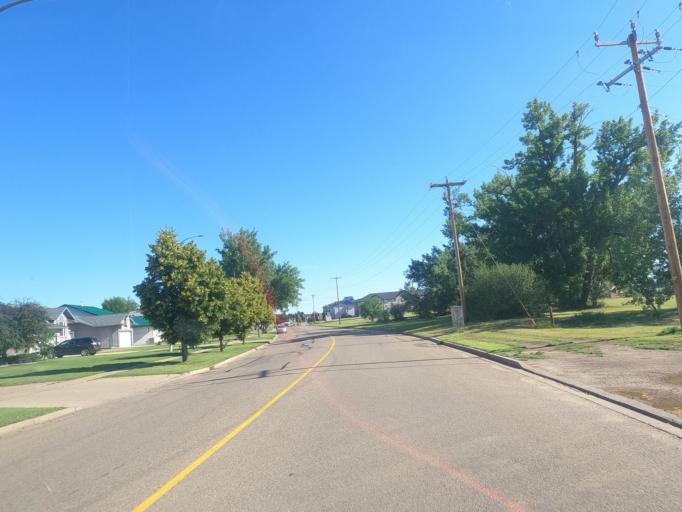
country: CA
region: Alberta
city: Brooks
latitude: 50.5811
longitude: -111.8999
